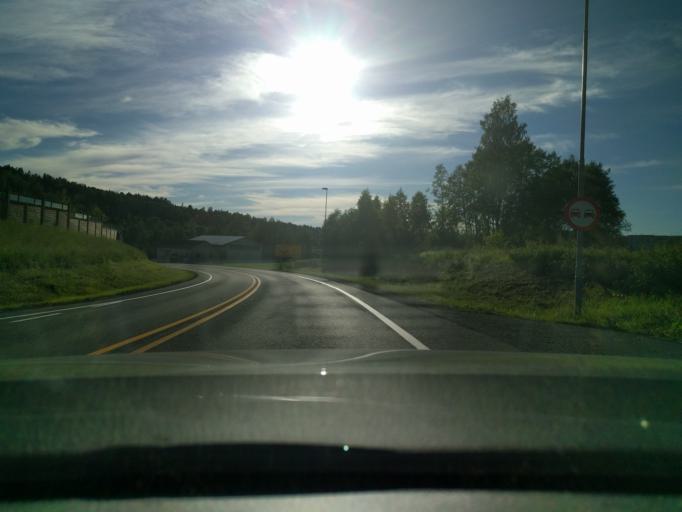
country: NO
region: Vestfold
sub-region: Holmestrand
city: Gullhaug
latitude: 59.5065
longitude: 10.1800
